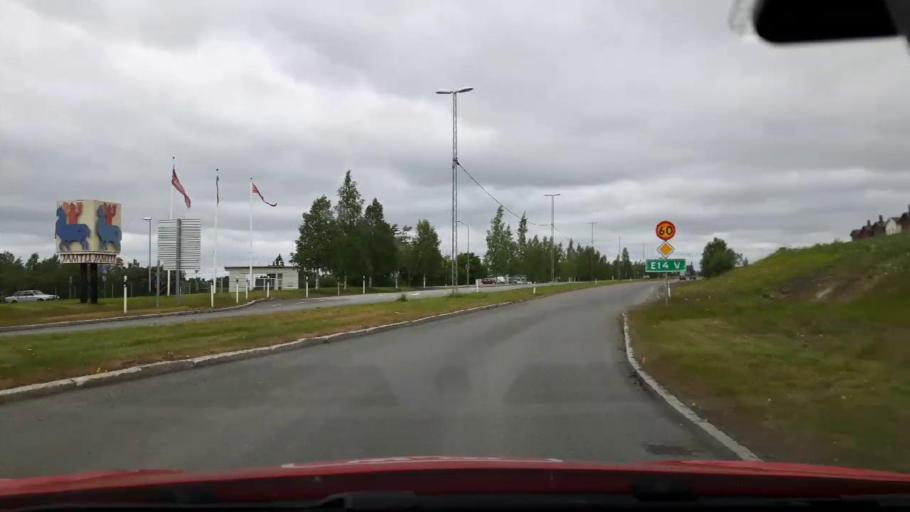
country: SE
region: Jaemtland
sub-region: OEstersunds Kommun
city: Ostersund
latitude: 63.1863
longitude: 14.6396
